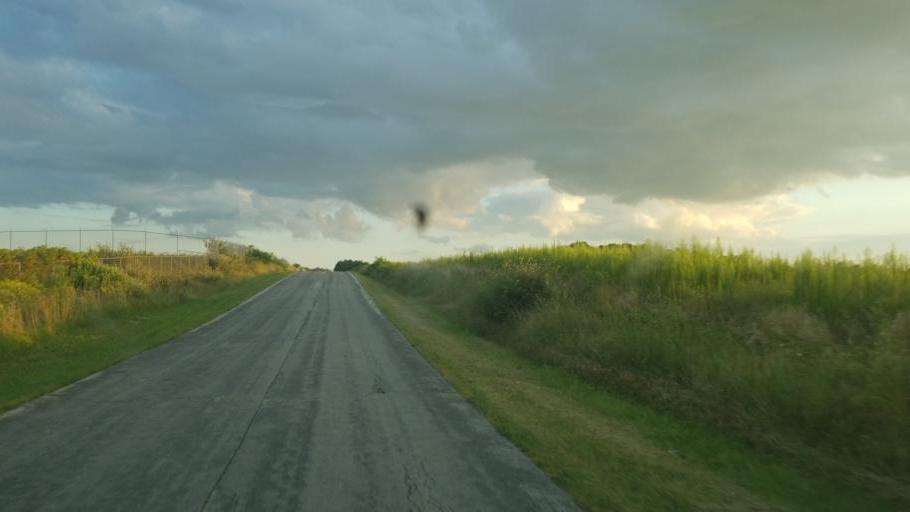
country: US
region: Ohio
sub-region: Richland County
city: Mansfield
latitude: 40.8371
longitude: -82.5329
